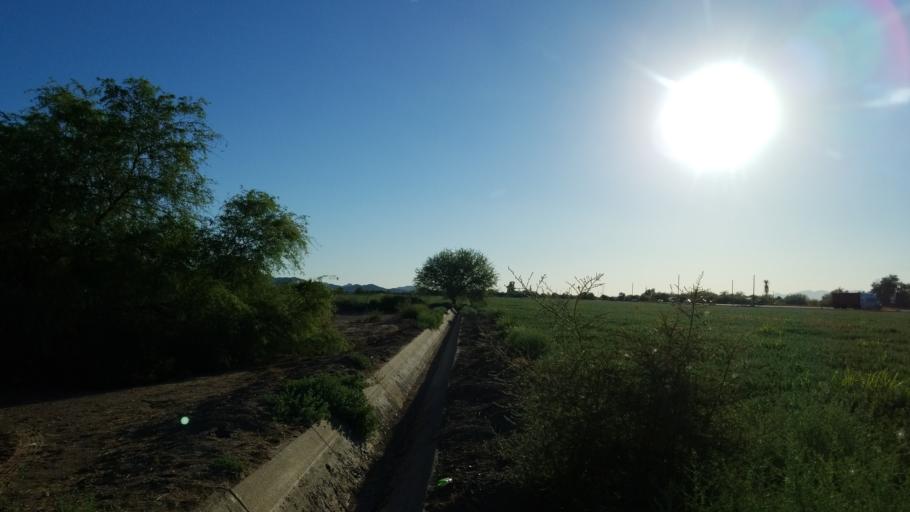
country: US
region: Arizona
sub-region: Maricopa County
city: Laveen
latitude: 33.3764
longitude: -112.2378
